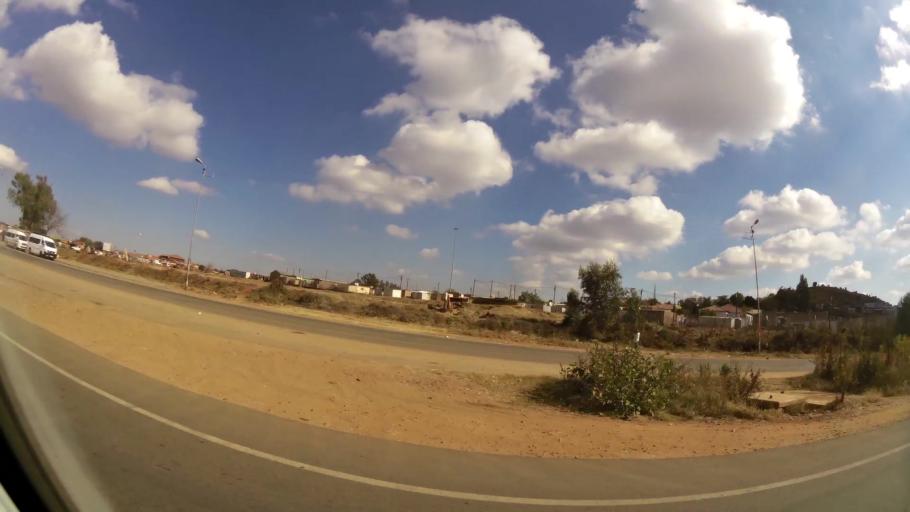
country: ZA
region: Gauteng
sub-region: City of Tshwane Metropolitan Municipality
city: Cullinan
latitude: -25.6973
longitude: 28.4200
